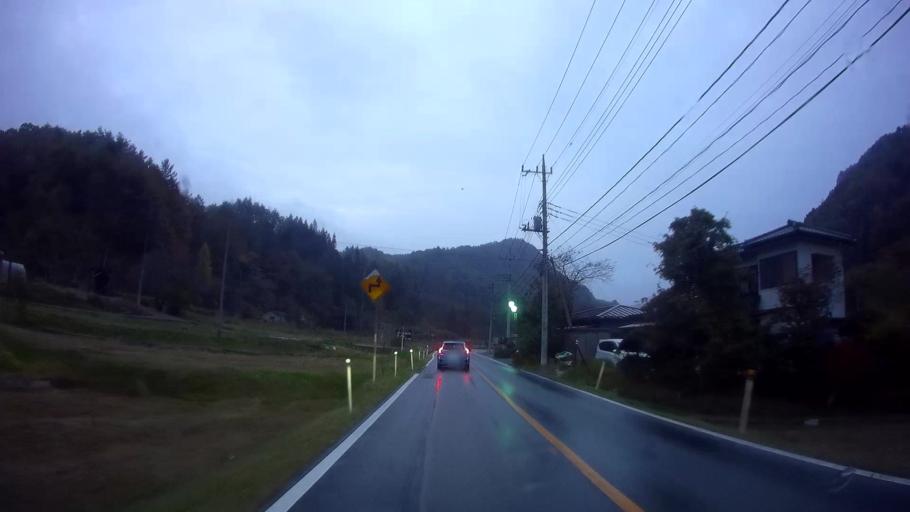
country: JP
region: Gunma
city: Nakanojomachi
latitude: 36.5232
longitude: 138.7827
